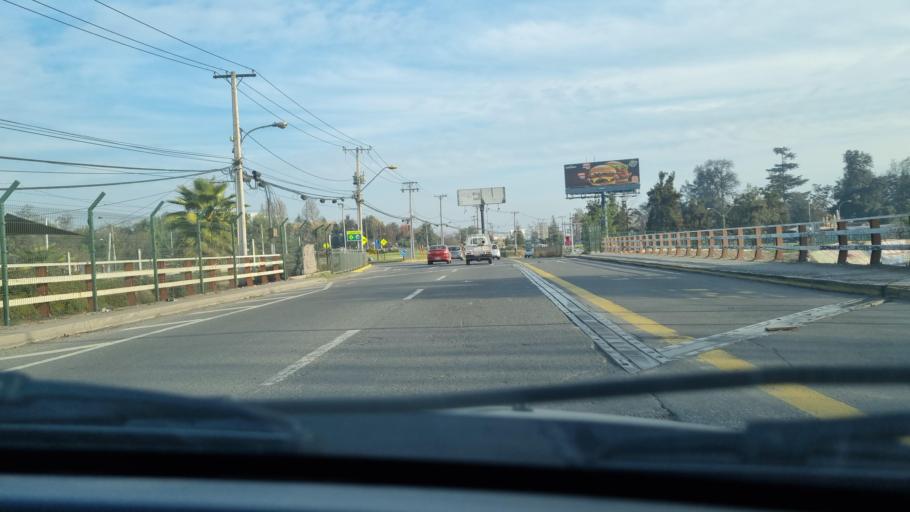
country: CL
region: Santiago Metropolitan
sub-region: Provincia de Santiago
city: Lo Prado
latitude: -33.4916
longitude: -70.7549
